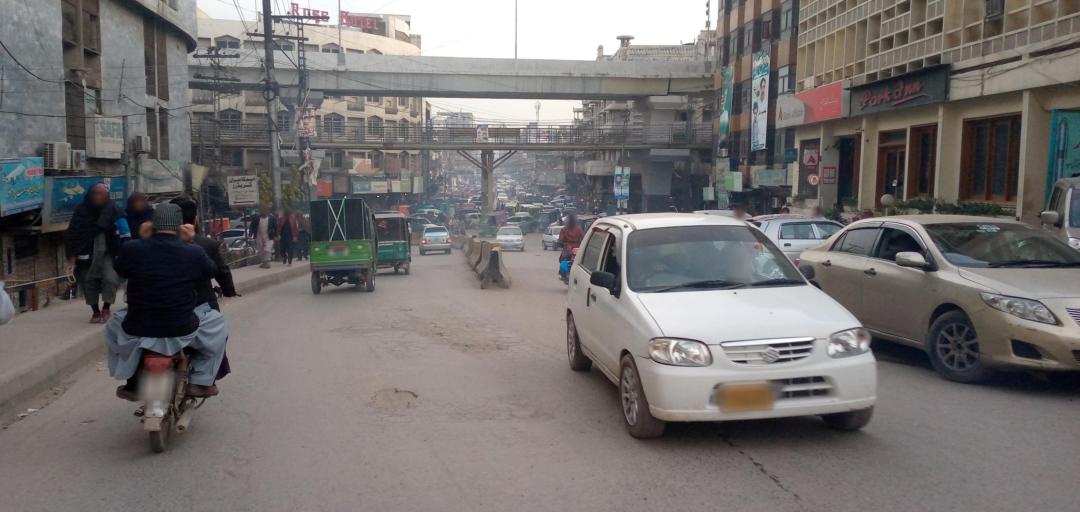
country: PK
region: Khyber Pakhtunkhwa
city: Peshawar
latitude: 34.0093
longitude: 71.5632
